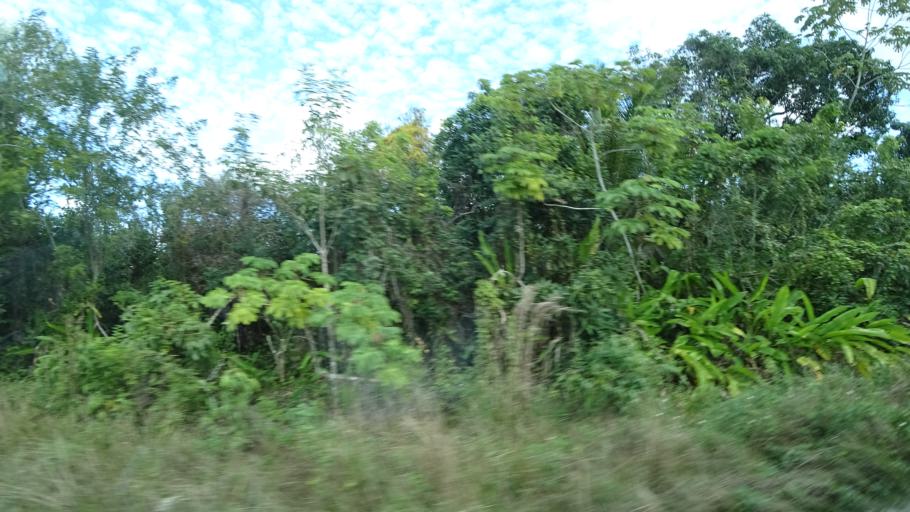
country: BZ
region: Belize
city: Belize City
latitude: 17.5639
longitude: -88.4060
